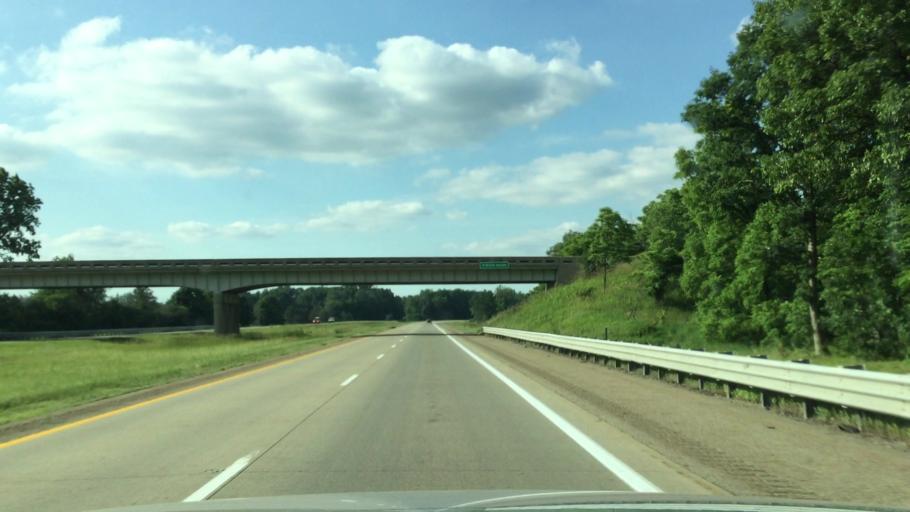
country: US
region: Michigan
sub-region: Calhoun County
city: Marshall
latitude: 42.1305
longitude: -84.9952
